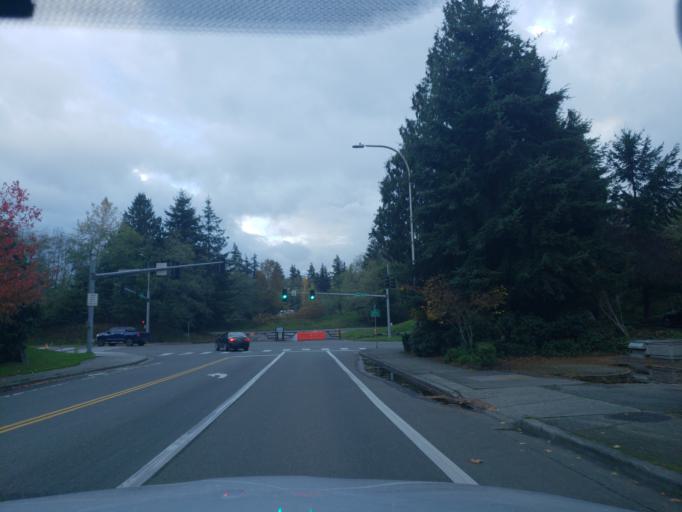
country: US
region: Washington
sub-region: Snohomish County
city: Mukilteo
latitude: 47.9376
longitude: -122.2679
